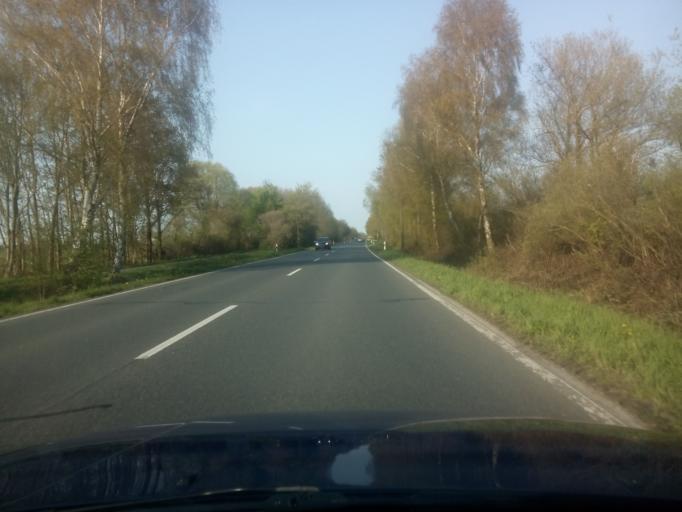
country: DE
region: Lower Saxony
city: Ritterhude
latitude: 53.1751
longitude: 8.7636
